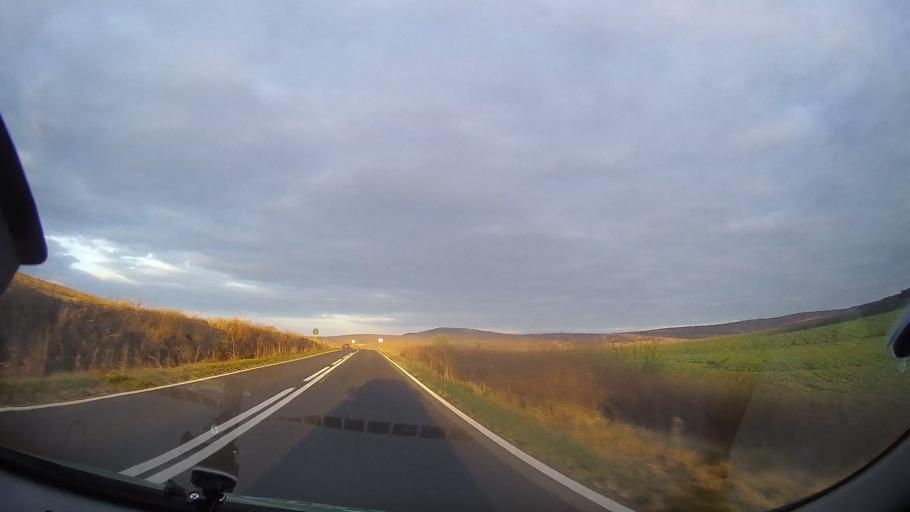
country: RO
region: Tulcea
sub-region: Comuna Nalbant
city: Nicolae Balcescu
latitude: 44.9686
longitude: 28.5362
